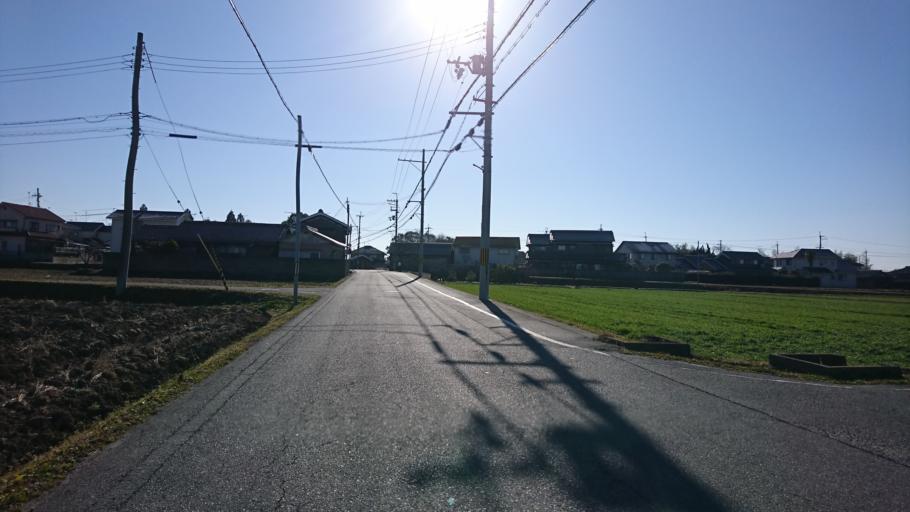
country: JP
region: Hyogo
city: Miki
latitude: 34.7441
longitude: 134.9393
